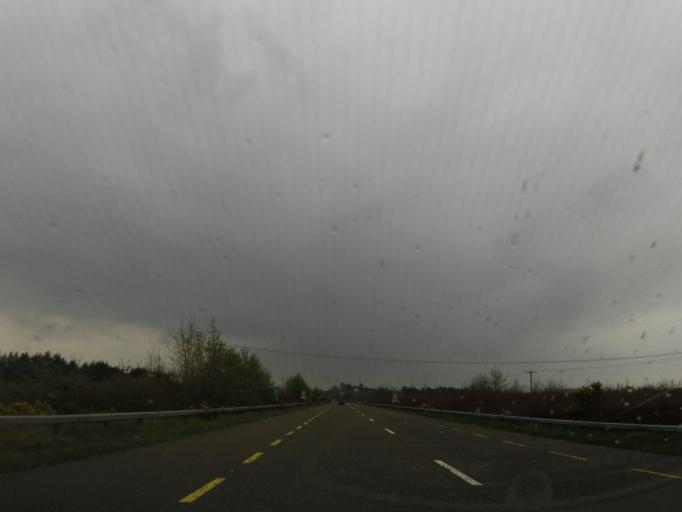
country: IE
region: Connaught
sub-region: Maigh Eo
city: Claremorris
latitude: 53.7304
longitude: -8.9782
